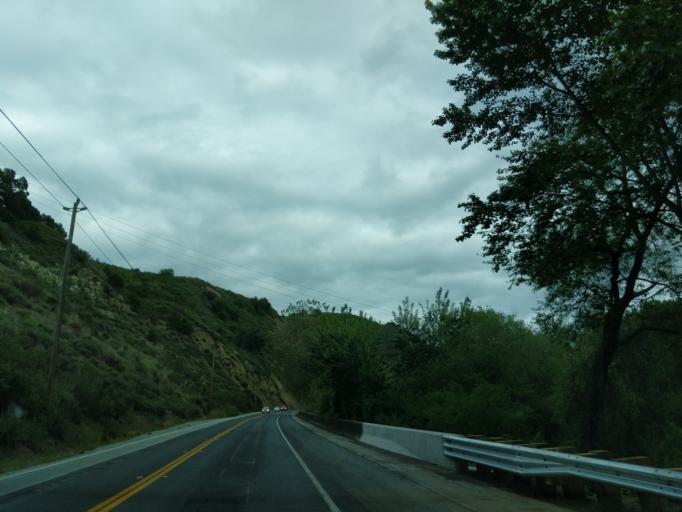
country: US
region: California
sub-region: San Benito County
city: Aromas
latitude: 36.9145
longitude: -121.6574
